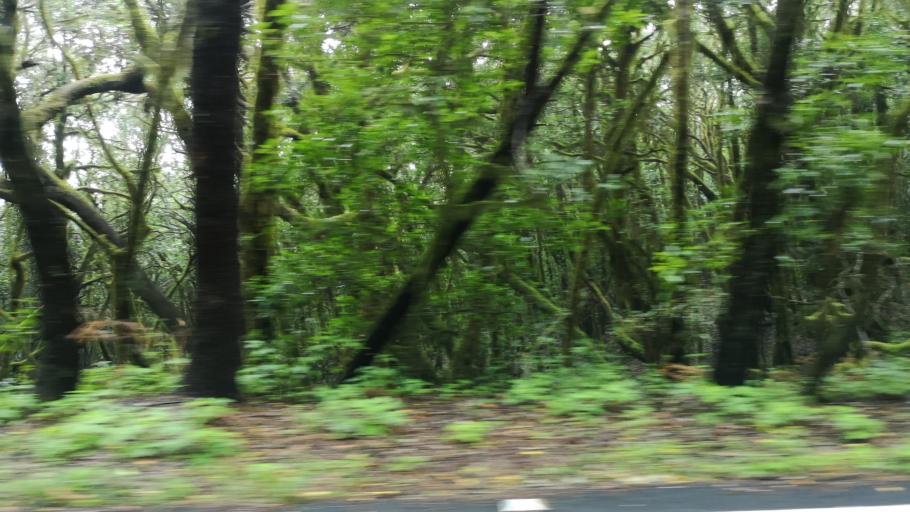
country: ES
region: Canary Islands
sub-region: Provincia de Santa Cruz de Tenerife
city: Vallehermosa
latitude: 28.1472
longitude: -17.2899
